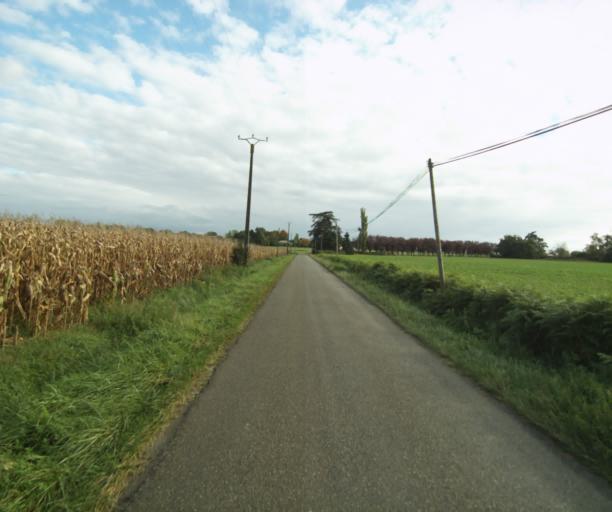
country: FR
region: Midi-Pyrenees
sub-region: Departement du Gers
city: Eauze
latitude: 43.8714
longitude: 0.0908
